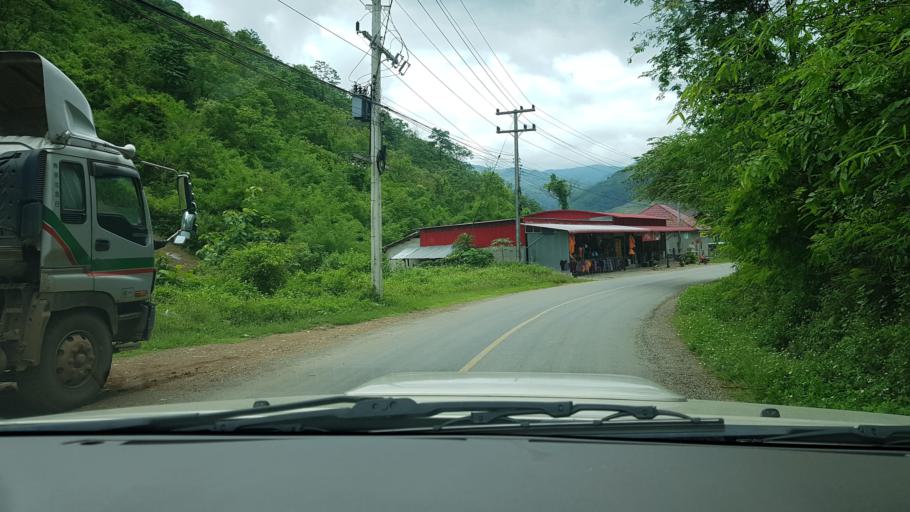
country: TH
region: Nan
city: Chaloem Phra Kiat
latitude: 19.9707
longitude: 101.2676
